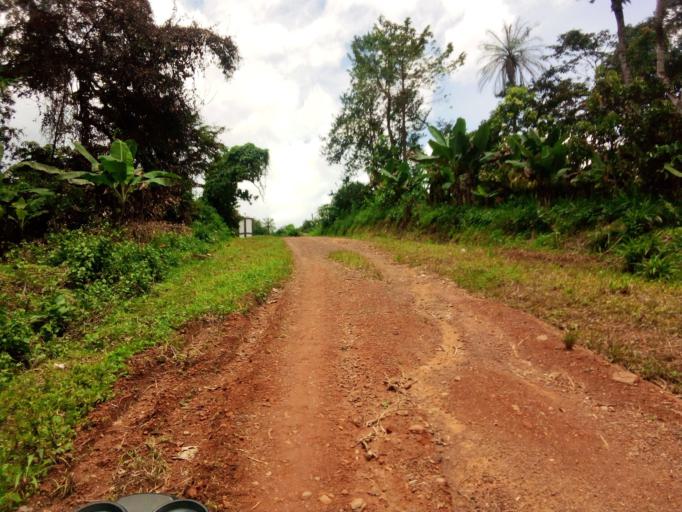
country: SL
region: Eastern Province
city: Giehun
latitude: 8.5573
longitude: -10.9866
